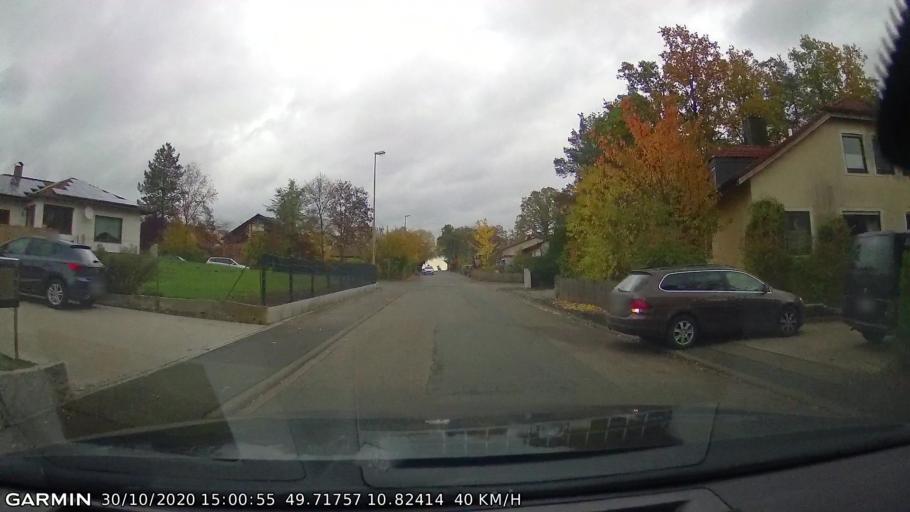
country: DE
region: Bavaria
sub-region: Regierungsbezirk Mittelfranken
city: Hochstadt an der Aisch
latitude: 49.7176
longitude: 10.8244
